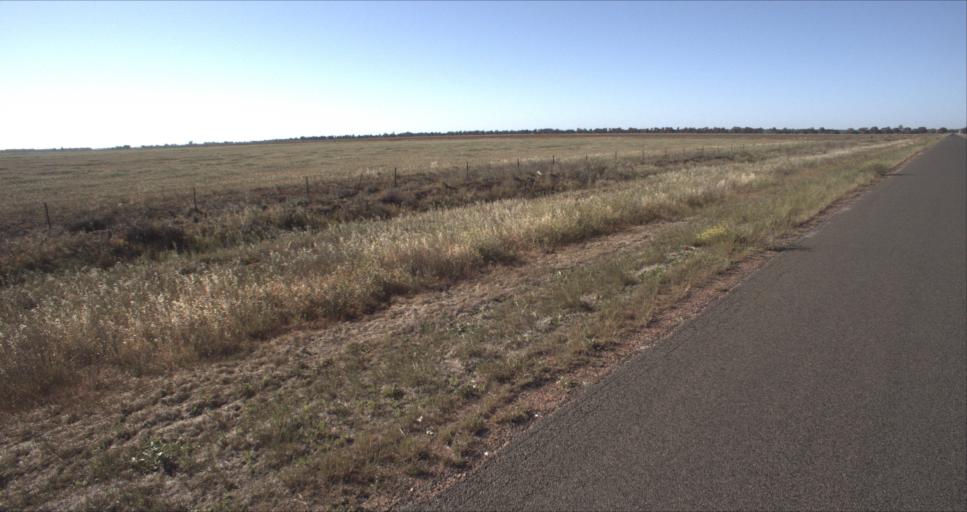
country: AU
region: New South Wales
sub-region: Leeton
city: Leeton
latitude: -34.5648
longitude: 146.2646
